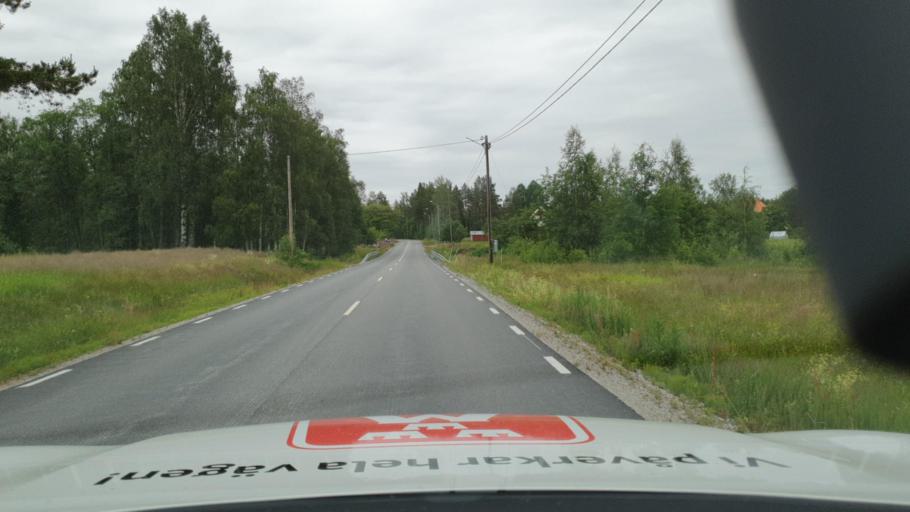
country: SE
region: Vaesterbotten
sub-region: Nordmalings Kommun
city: Nordmaling
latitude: 63.5004
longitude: 19.3255
